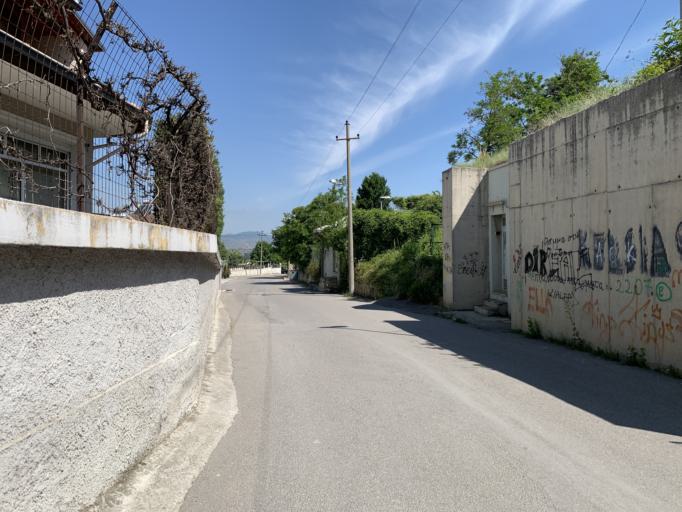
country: AL
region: Korce
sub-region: Rrethi i Korces
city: Korce
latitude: 40.6182
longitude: 20.7870
